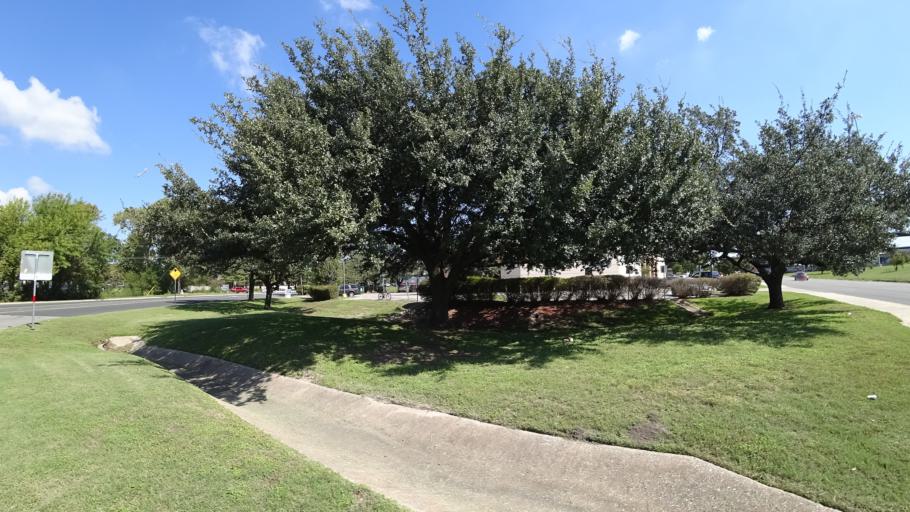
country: US
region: Texas
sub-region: Travis County
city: Austin
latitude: 30.3216
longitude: -97.7109
